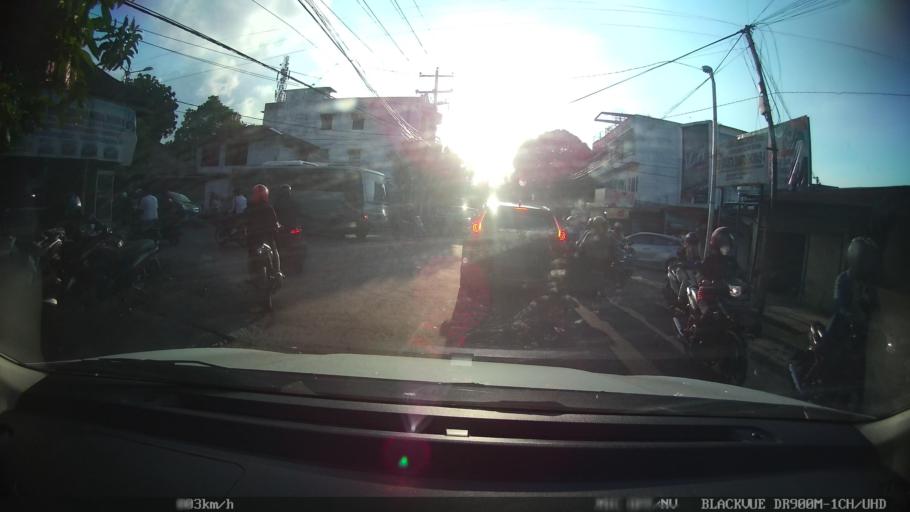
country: ID
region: North Sumatra
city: Medan
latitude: 3.6028
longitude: 98.6616
